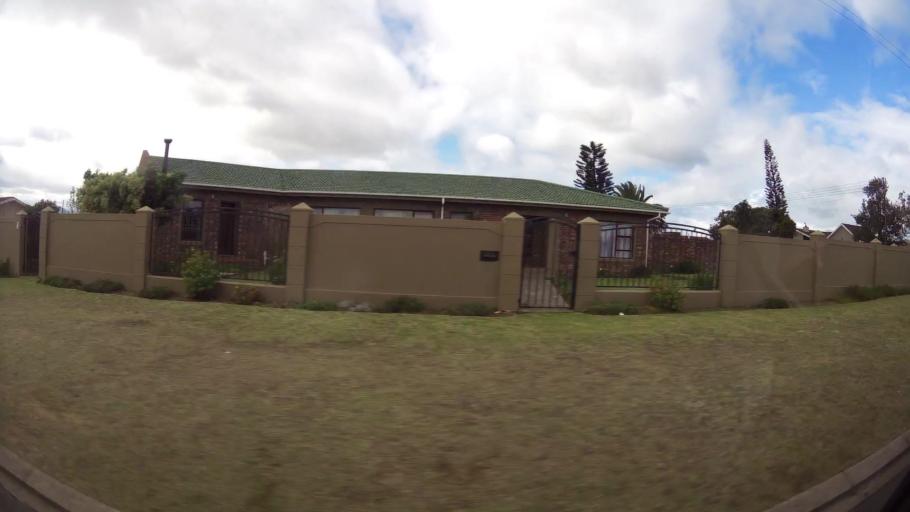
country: ZA
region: Western Cape
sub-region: Eden District Municipality
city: George
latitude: -34.0077
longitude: 22.4397
